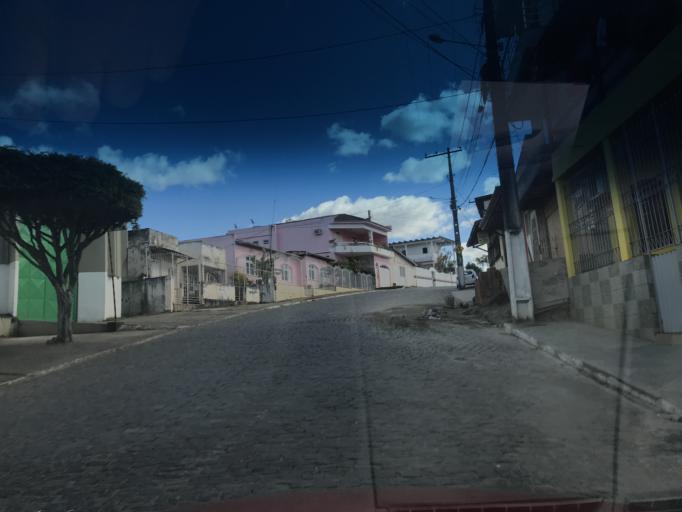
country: BR
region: Bahia
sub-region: Gandu
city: Gandu
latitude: -13.7460
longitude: -39.4900
